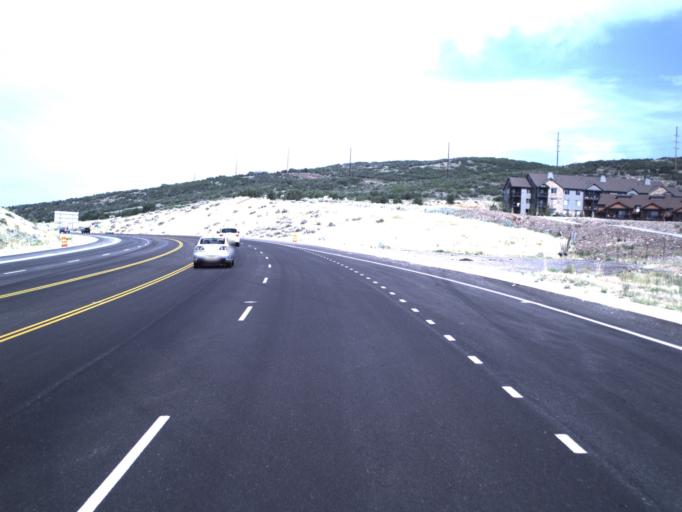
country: US
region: Utah
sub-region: Summit County
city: Park City
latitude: 40.6795
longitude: -111.4339
